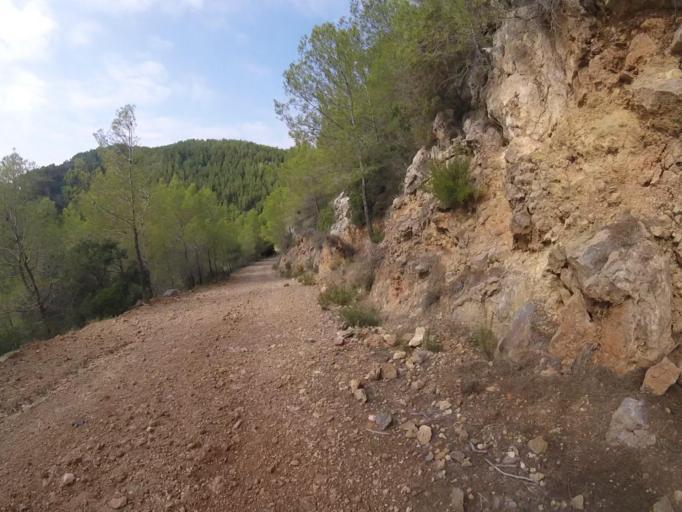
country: ES
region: Valencia
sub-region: Provincia de Castello
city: Benicassim
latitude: 40.0868
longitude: 0.0495
